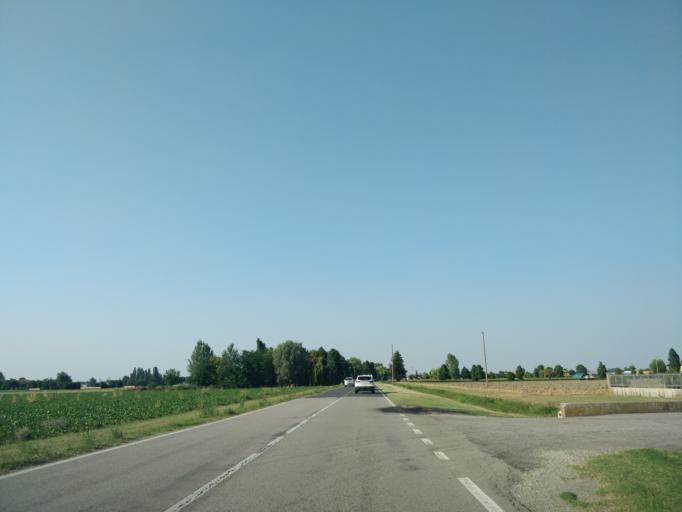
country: IT
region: Emilia-Romagna
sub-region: Provincia di Bologna
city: Argelato
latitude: 44.6256
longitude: 11.3384
